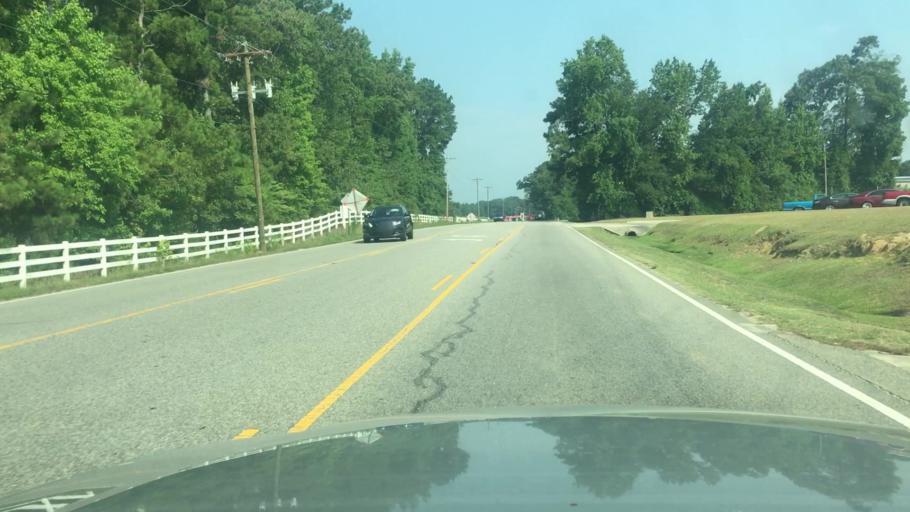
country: US
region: North Carolina
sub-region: Cumberland County
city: Hope Mills
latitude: 34.9302
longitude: -78.9149
